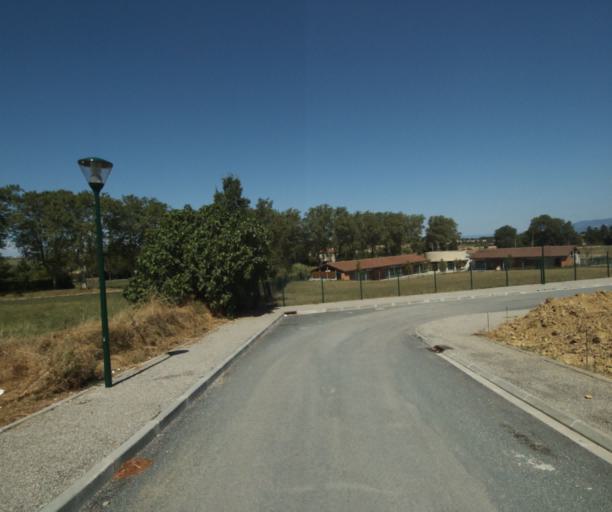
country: FR
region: Midi-Pyrenees
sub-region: Departement de la Haute-Garonne
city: Saint-Felix-Lauragais
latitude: 43.4888
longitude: 1.9028
